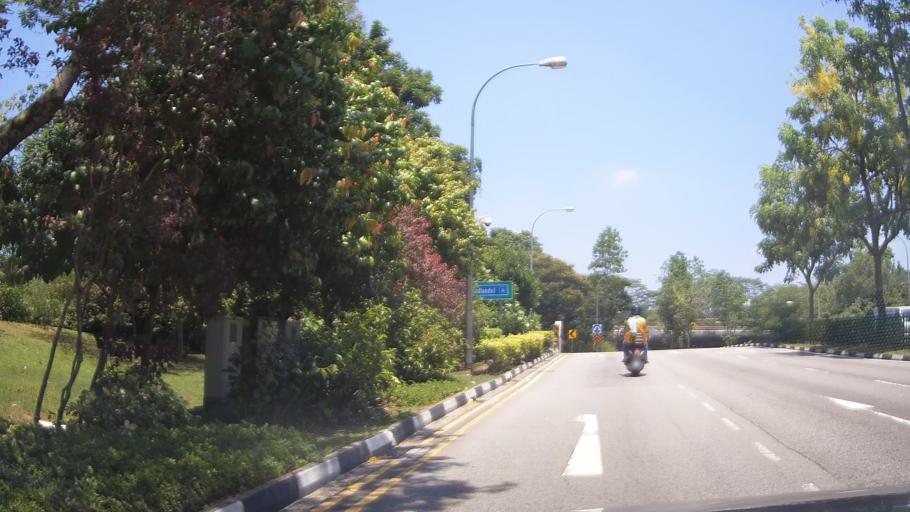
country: MY
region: Johor
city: Johor Bahru
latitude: 1.3757
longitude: 103.7757
